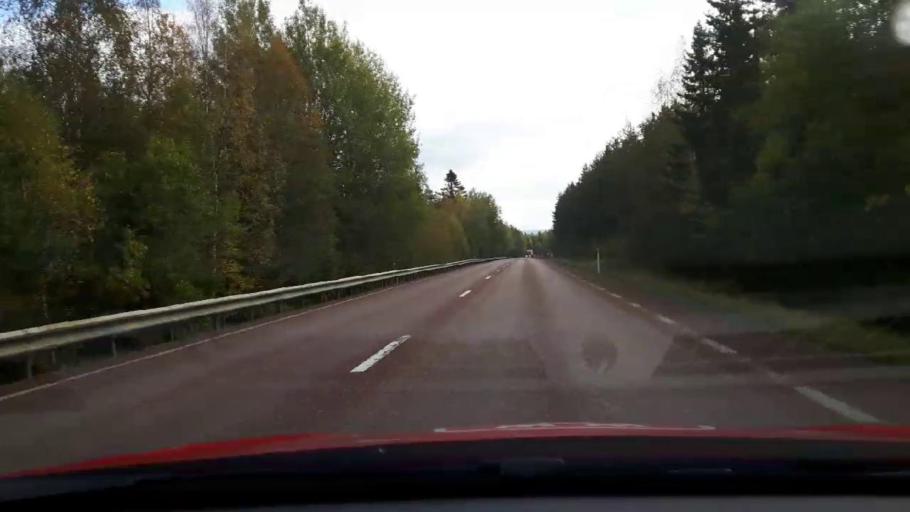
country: SE
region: Gaevleborg
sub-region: Ljusdals Kommun
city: Jaervsoe
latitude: 61.6367
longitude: 16.2553
